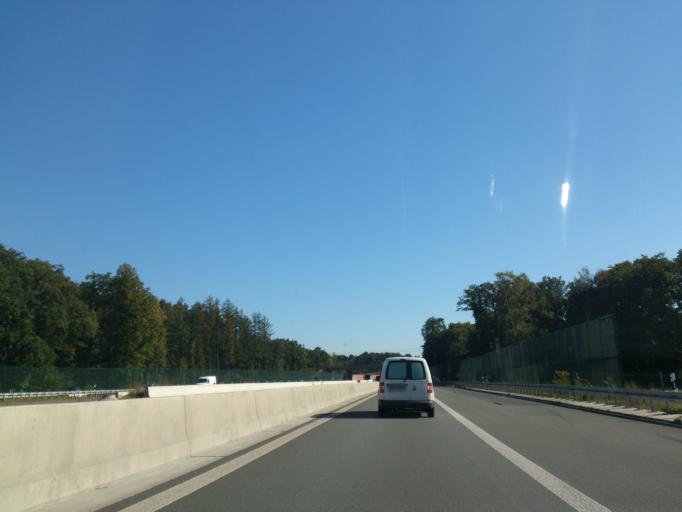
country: DE
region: North Rhine-Westphalia
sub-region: Regierungsbezirk Detmold
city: Bielefeld
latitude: 51.9720
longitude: 8.4835
